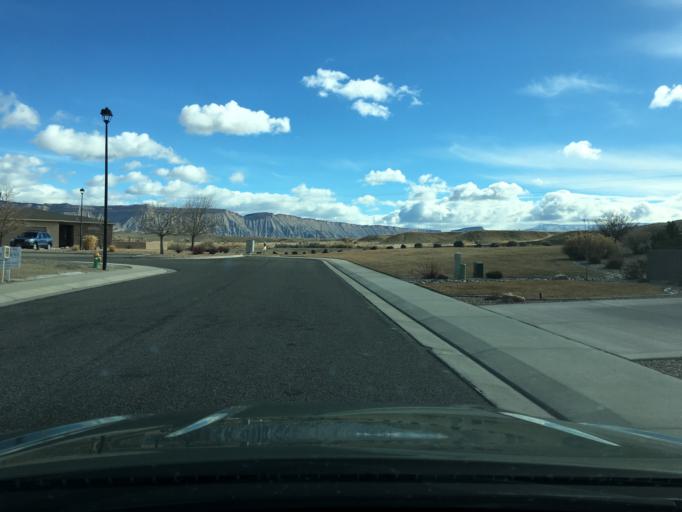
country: US
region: Colorado
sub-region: Mesa County
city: Grand Junction
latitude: 39.1317
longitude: -108.5534
